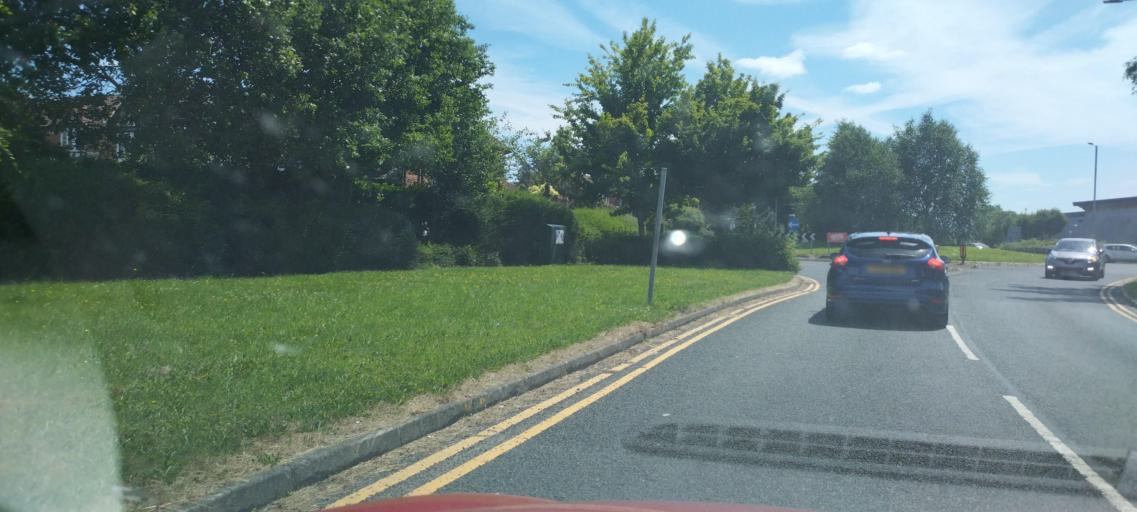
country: GB
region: England
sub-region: Borough of Bolton
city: Horwich
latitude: 53.5848
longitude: -2.5334
